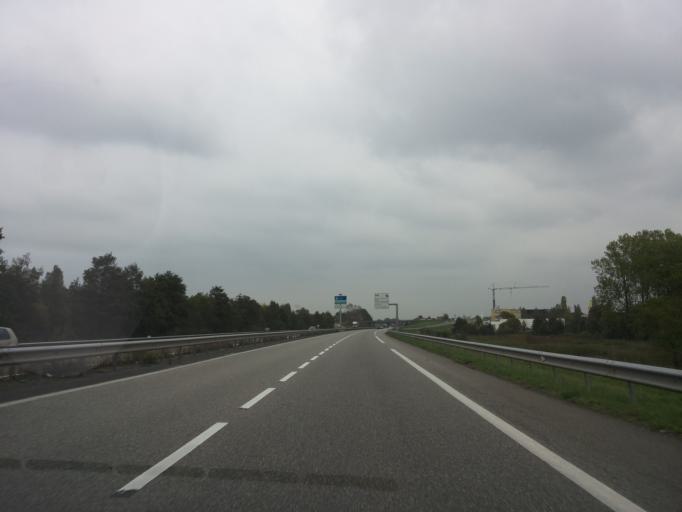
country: FR
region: Lorraine
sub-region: Departement de la Moselle
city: Sarrebourg
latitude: 48.7320
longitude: 7.0739
